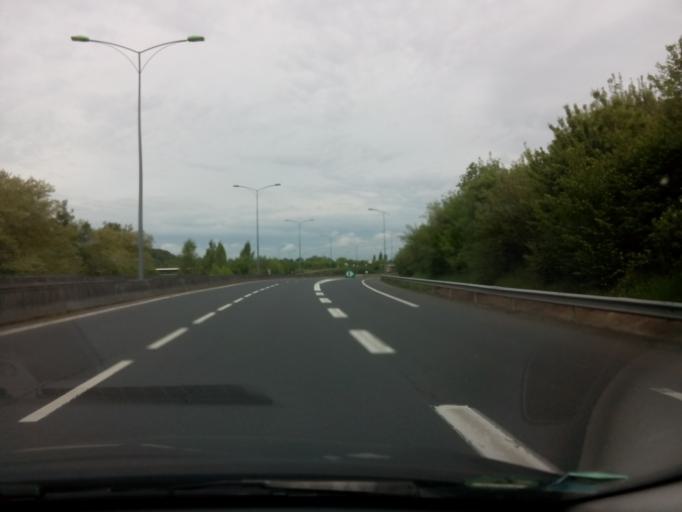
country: FR
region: Limousin
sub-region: Departement de la Correze
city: Varetz
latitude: 45.1659
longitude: 1.4705
